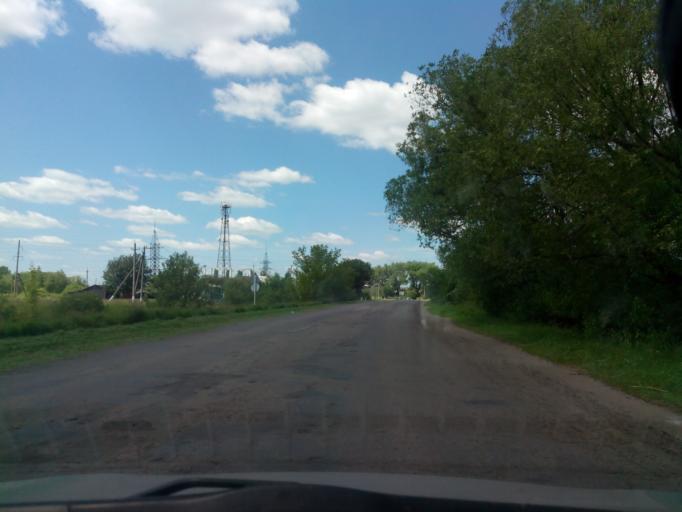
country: RU
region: Voronezj
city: Ternovka
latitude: 51.6764
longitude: 41.6057
